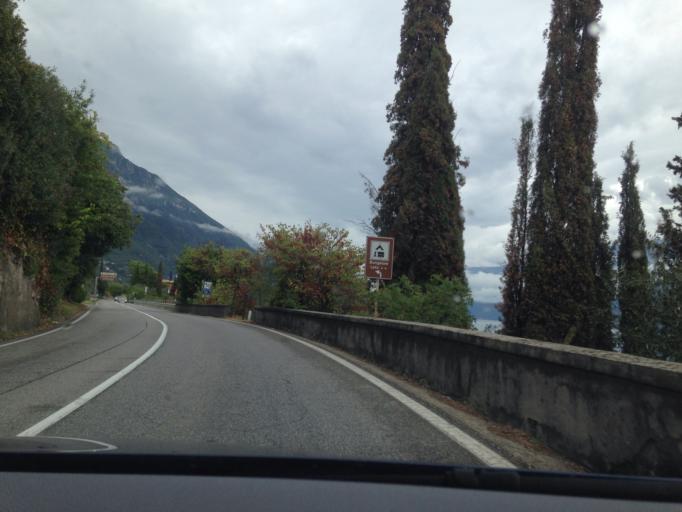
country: IT
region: Lombardy
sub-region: Provincia di Brescia
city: Gargnano
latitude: 45.6678
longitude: 10.6490
